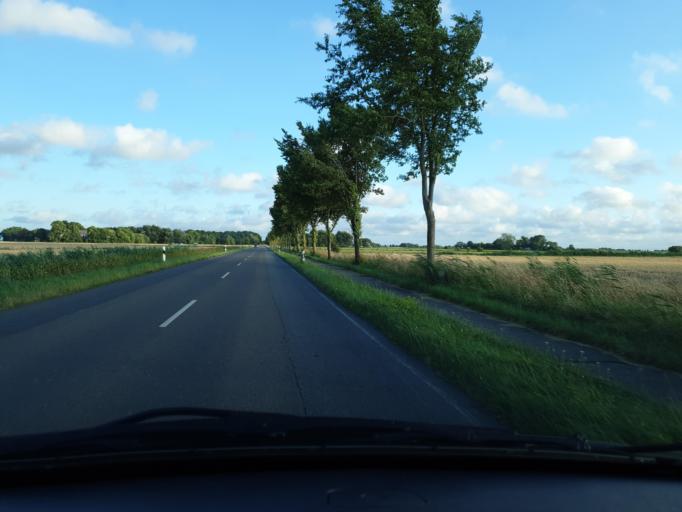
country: DE
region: Schleswig-Holstein
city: Wohrden
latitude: 54.1382
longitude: 9.0166
